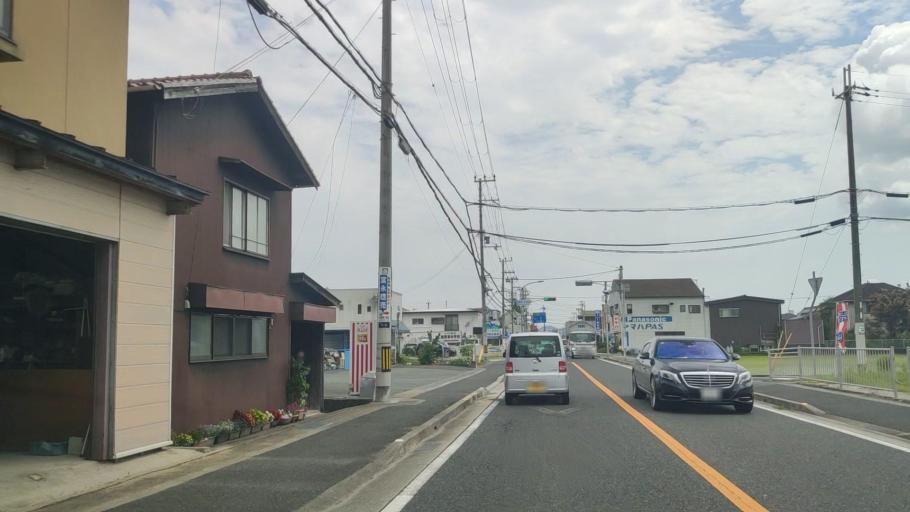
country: JP
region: Hyogo
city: Tatsunocho-tominaga
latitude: 34.8678
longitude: 134.5539
